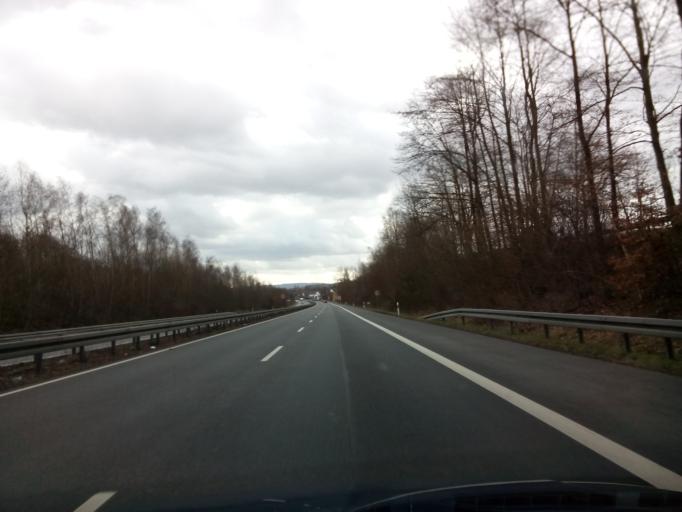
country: DE
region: Lower Saxony
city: Osnabrueck
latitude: 52.3086
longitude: 8.0347
